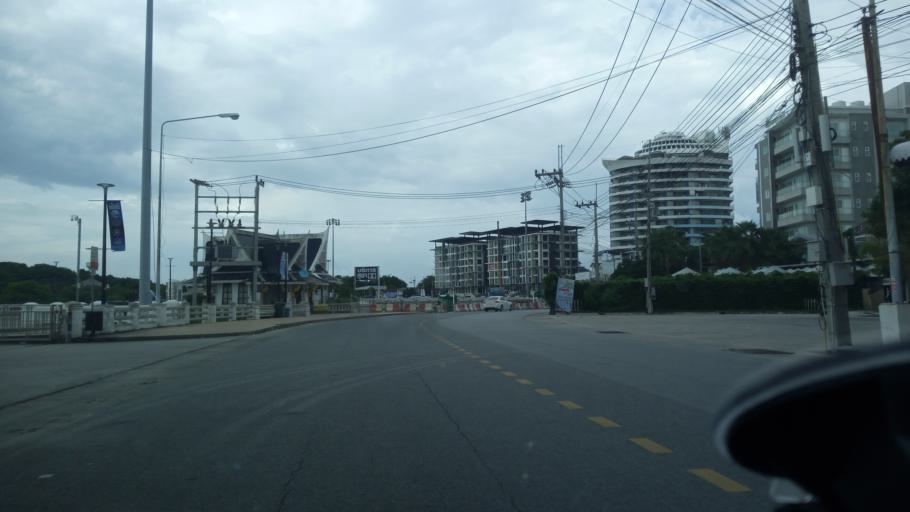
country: TH
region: Chon Buri
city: Chon Buri
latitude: 13.3034
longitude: 100.8993
